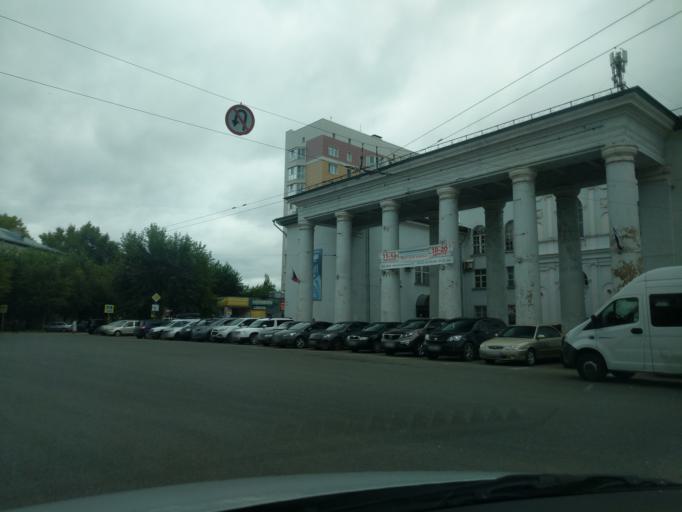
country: RU
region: Kirov
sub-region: Kirovo-Chepetskiy Rayon
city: Kirov
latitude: 58.6368
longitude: 49.6121
